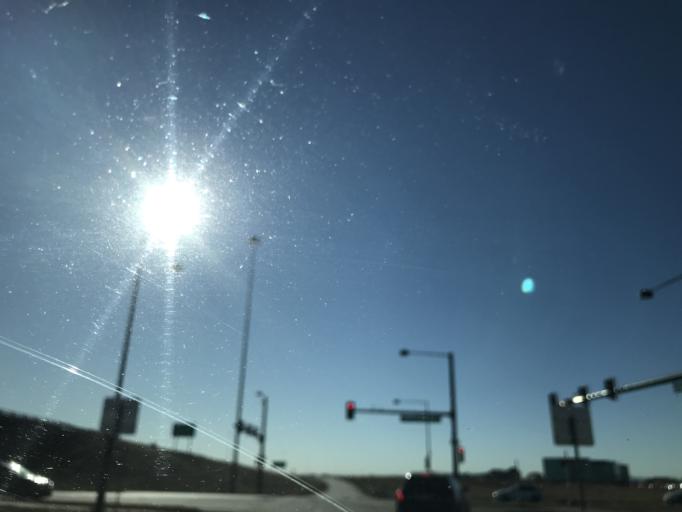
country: US
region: Colorado
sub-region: Adams County
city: Aurora
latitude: 39.7843
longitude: -104.7920
